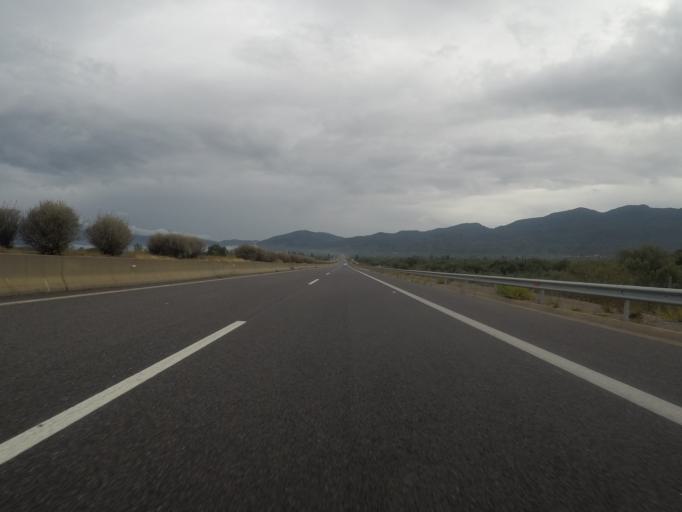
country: GR
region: Peloponnese
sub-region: Nomos Messinias
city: Meligalas
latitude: 37.2160
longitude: 22.0039
